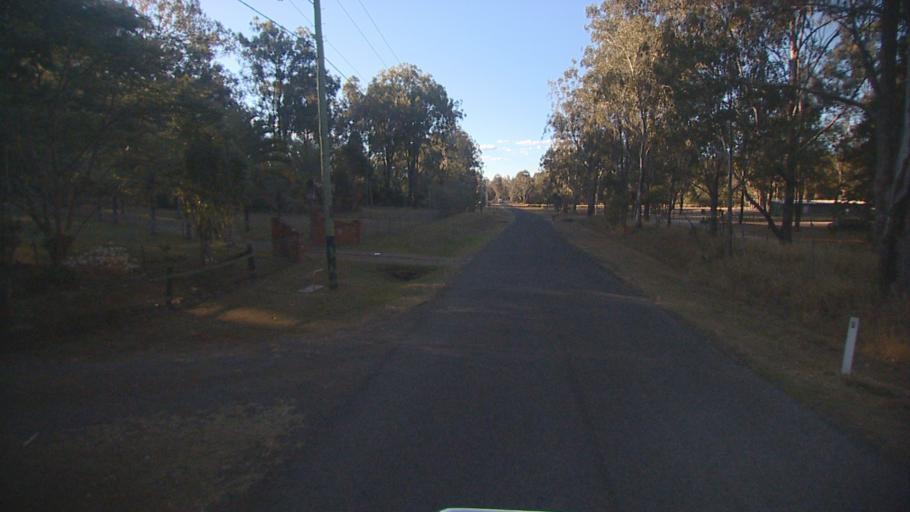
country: AU
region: Queensland
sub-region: Logan
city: Cedar Vale
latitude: -27.8669
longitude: 152.9764
